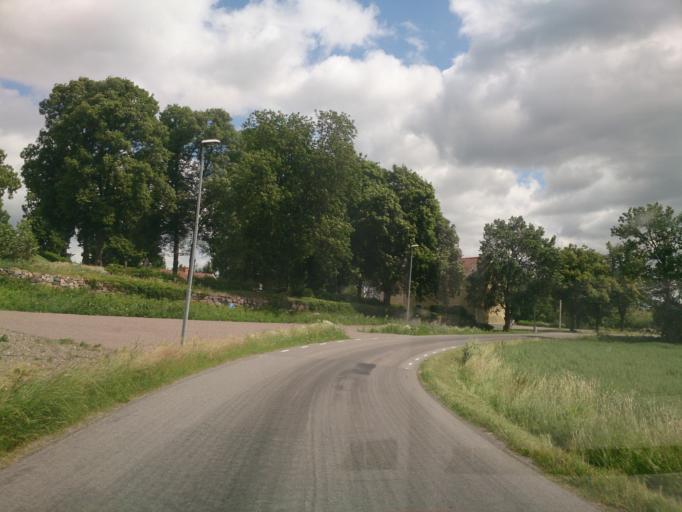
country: SE
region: OEstergoetland
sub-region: Norrkopings Kommun
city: Krokek
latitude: 58.5274
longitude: 16.4742
